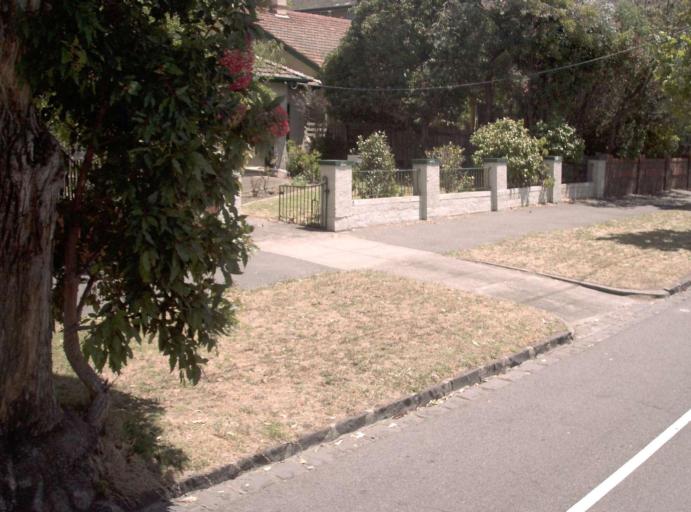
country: AU
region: Victoria
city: Ripponlea
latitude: -37.8819
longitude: 144.9956
